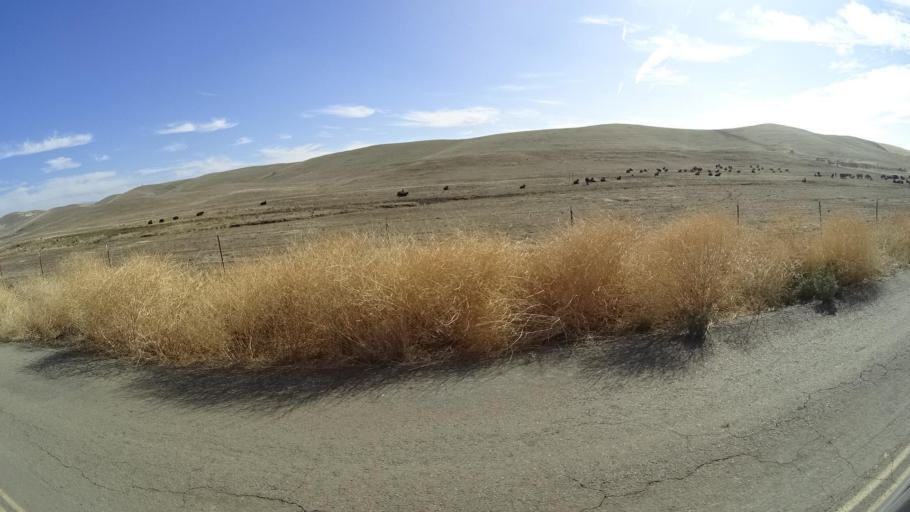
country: US
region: California
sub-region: Tulare County
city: Richgrove
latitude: 35.6298
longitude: -118.9727
